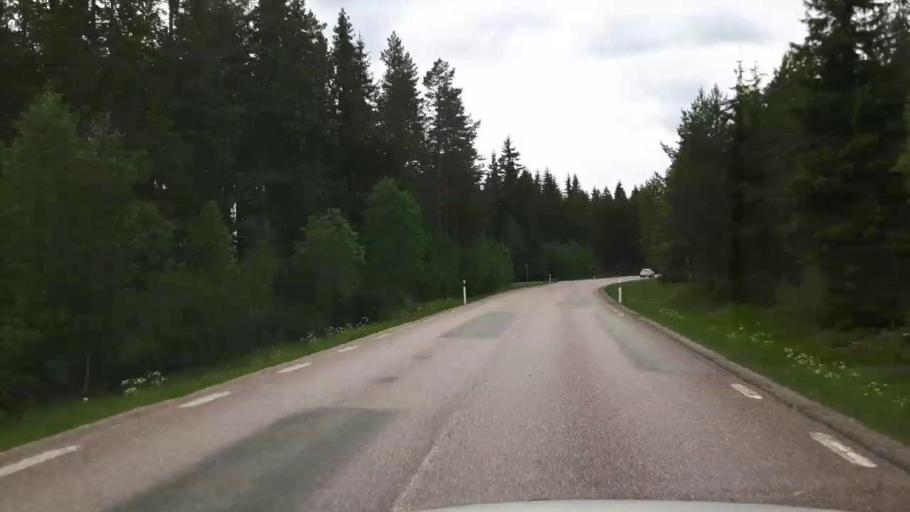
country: SE
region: Dalarna
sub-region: Hedemora Kommun
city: Brunna
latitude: 60.1677
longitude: 15.9947
